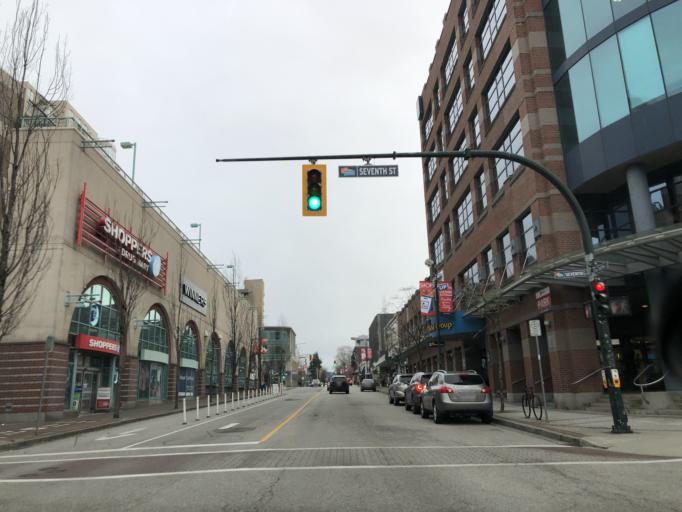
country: CA
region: British Columbia
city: New Westminster
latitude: 49.2122
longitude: -122.9219
